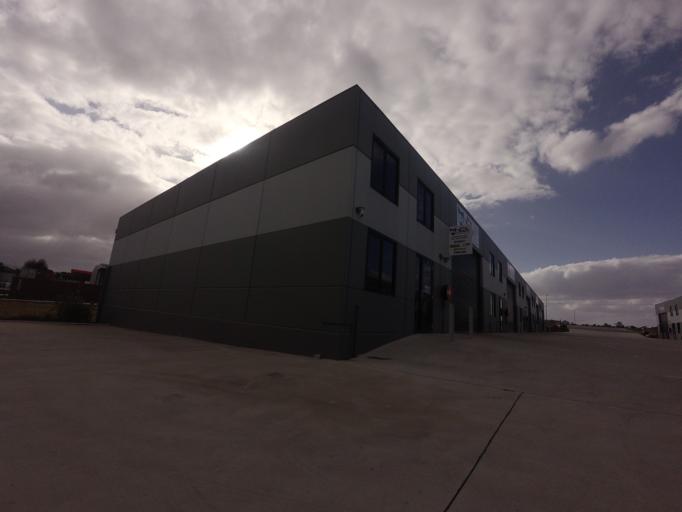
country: AU
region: Tasmania
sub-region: Clarence
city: Cambridge
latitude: -42.8339
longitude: 147.4590
